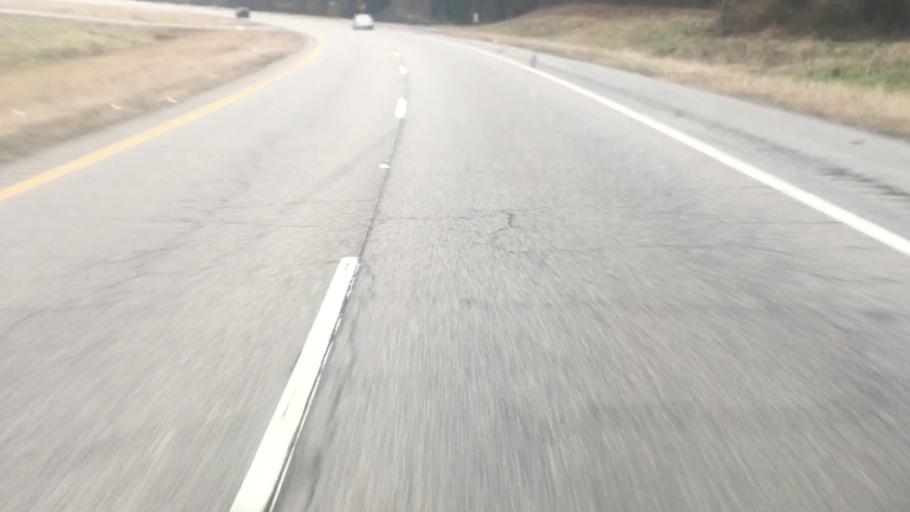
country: US
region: Alabama
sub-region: Walker County
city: Cordova
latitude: 33.8089
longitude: -87.1466
